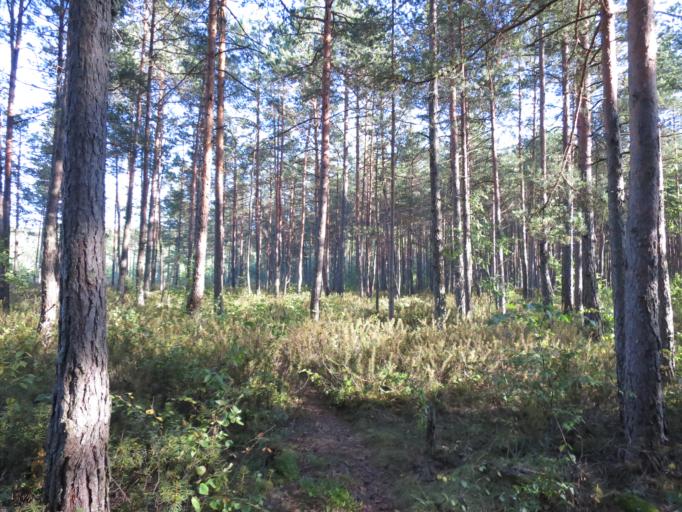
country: LV
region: Riga
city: Jaunciems
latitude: 57.0496
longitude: 24.2429
